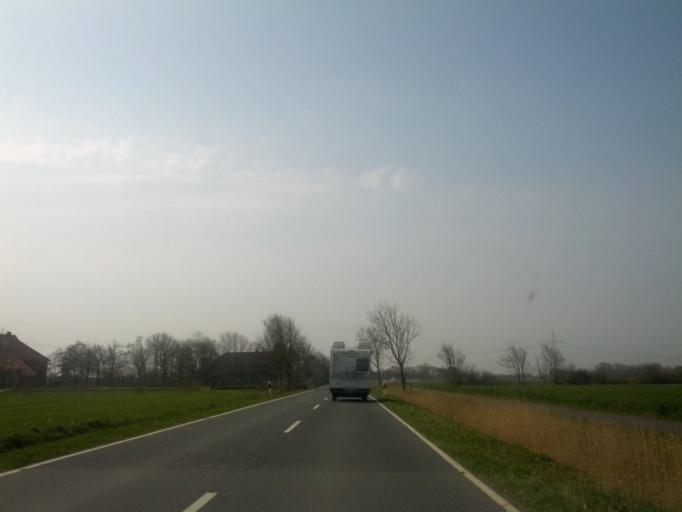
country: DE
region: Lower Saxony
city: Norden
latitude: 53.6193
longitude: 7.1901
